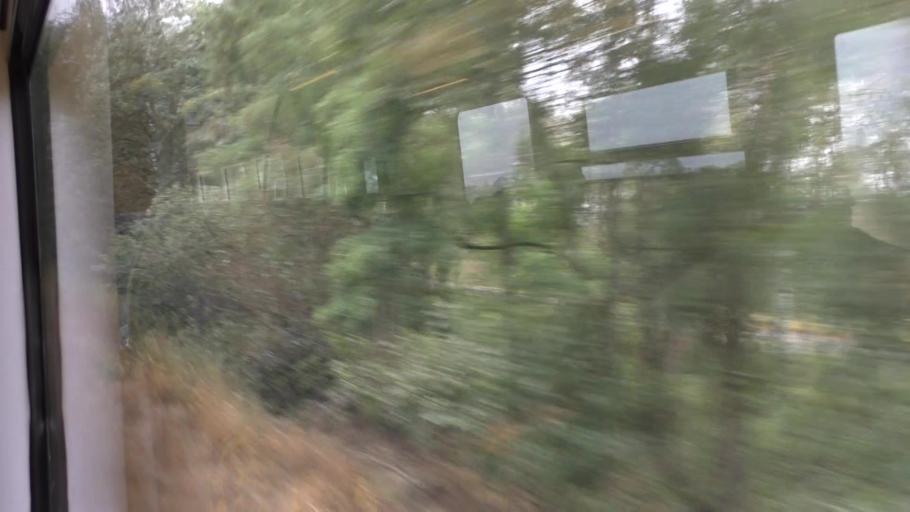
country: DE
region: Saxony
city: Goerlitz
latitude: 51.0883
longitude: 14.9737
